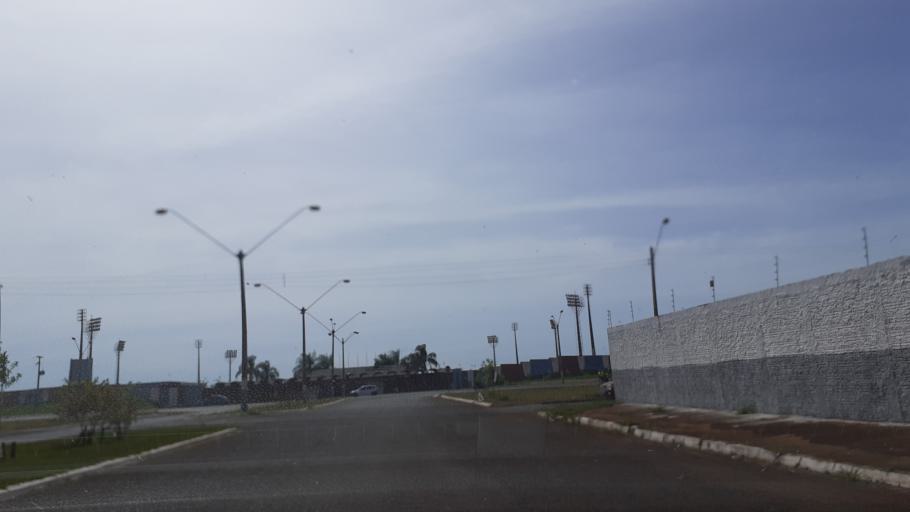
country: BR
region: Goias
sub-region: Itumbiara
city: Itumbiara
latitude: -18.4112
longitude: -49.2444
